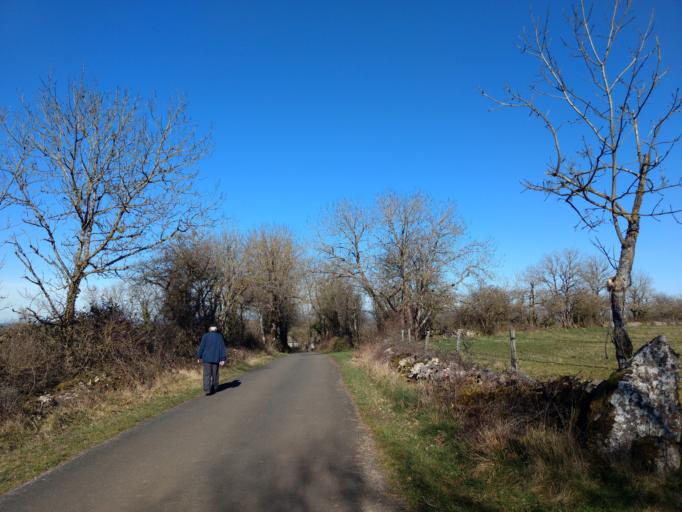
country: FR
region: Midi-Pyrenees
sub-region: Departement de l'Aveyron
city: Sebazac-Concoures
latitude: 44.4155
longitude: 2.5653
